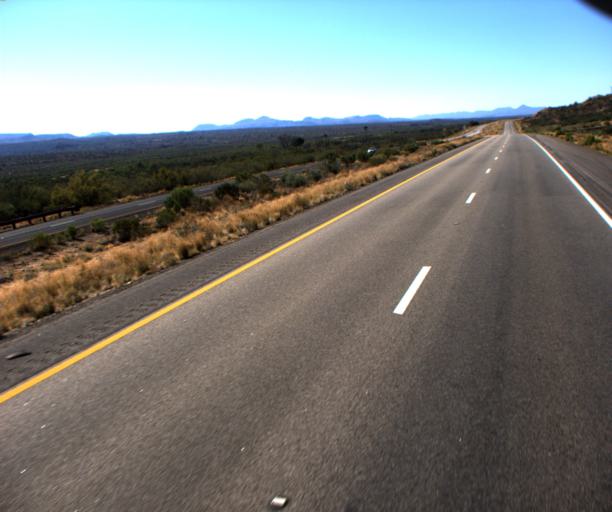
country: US
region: Arizona
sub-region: Yavapai County
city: Bagdad
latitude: 34.8351
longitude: -113.6326
